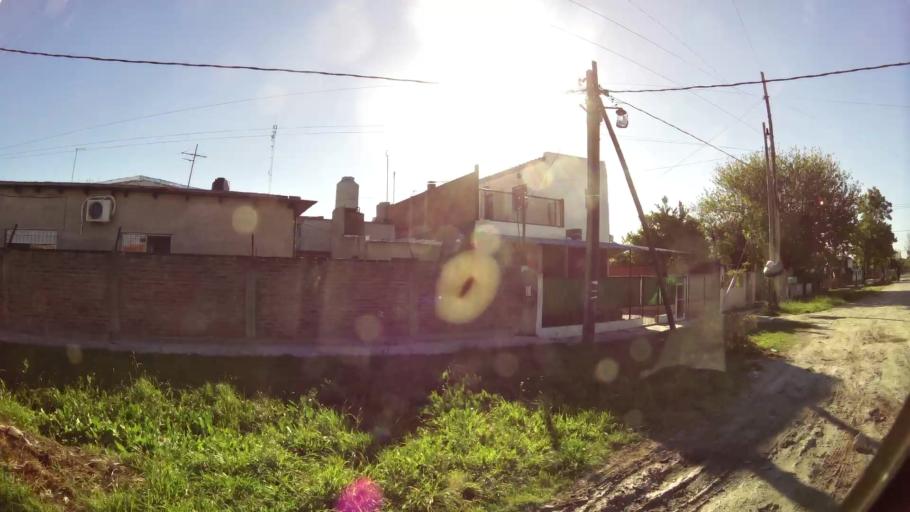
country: AR
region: Buenos Aires
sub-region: Partido de Quilmes
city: Quilmes
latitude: -34.7443
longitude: -58.3196
